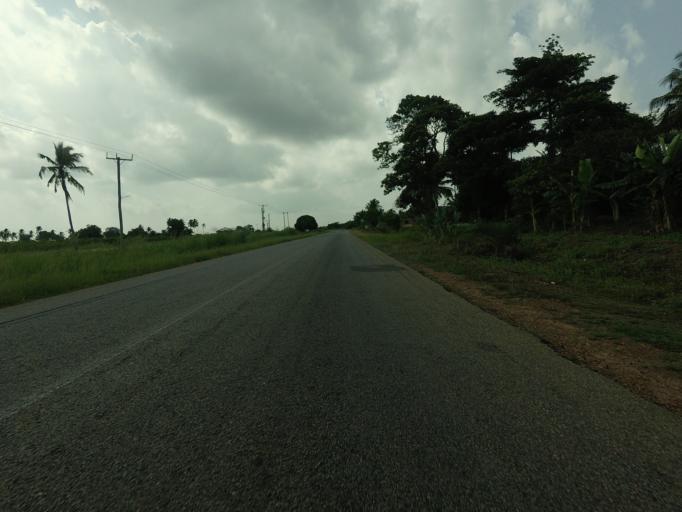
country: GH
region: Volta
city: Ho
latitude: 6.4304
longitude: 0.7322
